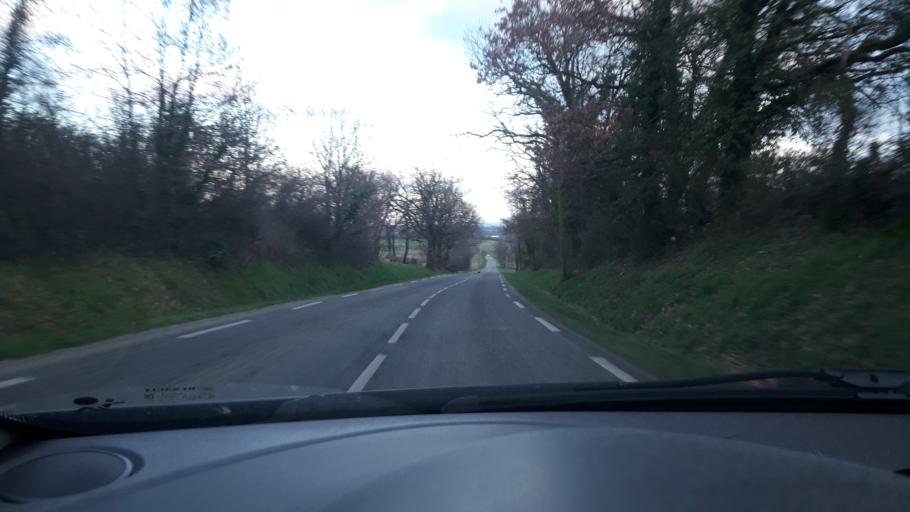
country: FR
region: Midi-Pyrenees
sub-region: Departement de la Haute-Garonne
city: Launac
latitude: 43.7447
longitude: 1.1370
